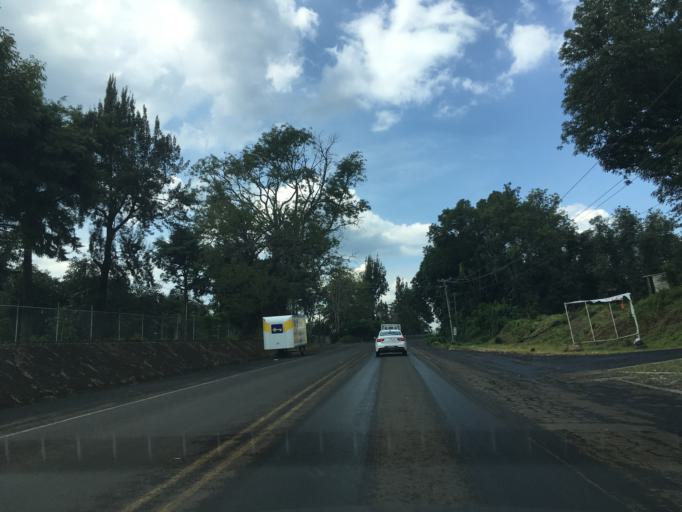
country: MX
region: Michoacan
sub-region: Tingueindin
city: Tingueindin
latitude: 19.7439
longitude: -102.4852
